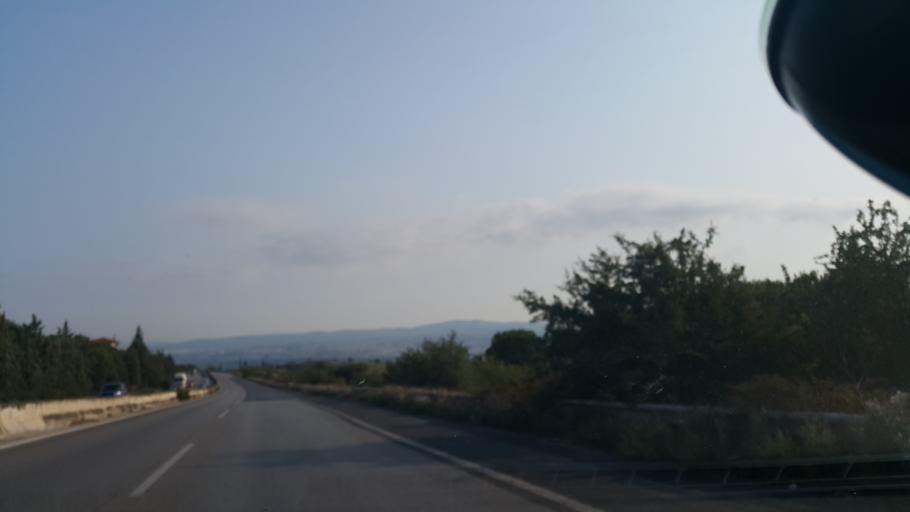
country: GR
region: Central Macedonia
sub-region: Nomos Thessalonikis
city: Kardia
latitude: 40.4770
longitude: 22.9930
